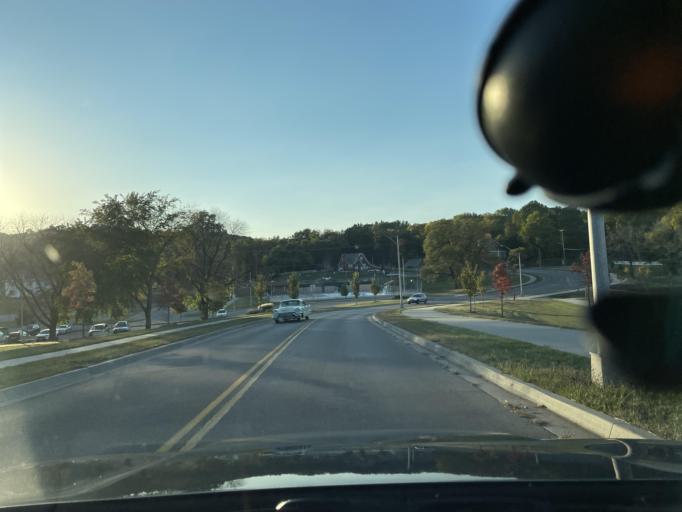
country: US
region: Missouri
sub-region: Buchanan County
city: Saint Joseph
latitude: 39.7979
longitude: -94.8428
